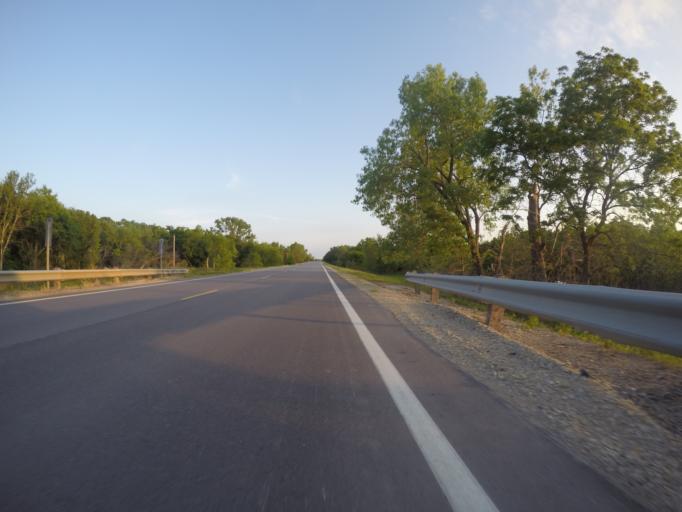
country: US
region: Kansas
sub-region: Riley County
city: Manhattan
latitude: 39.3003
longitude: -96.5566
